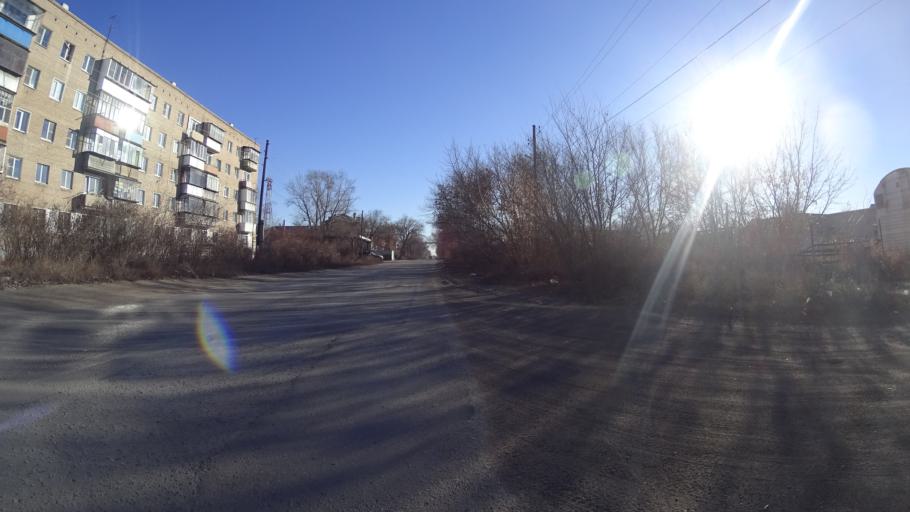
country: RU
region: Chelyabinsk
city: Troitsk
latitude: 54.1143
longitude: 61.5650
